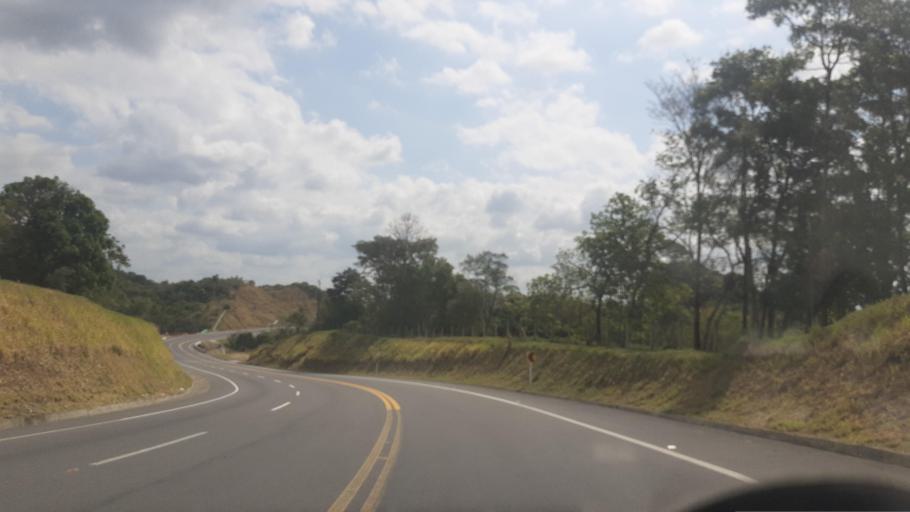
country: CO
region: Casanare
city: Monterrey
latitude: 4.8364
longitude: -72.8303
